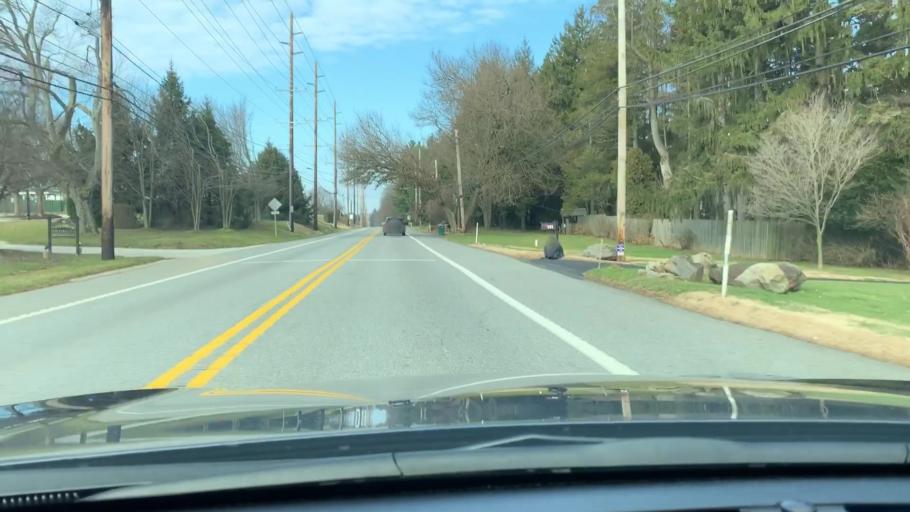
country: US
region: Pennsylvania
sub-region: Chester County
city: Paoli
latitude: 40.0257
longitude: -75.4618
